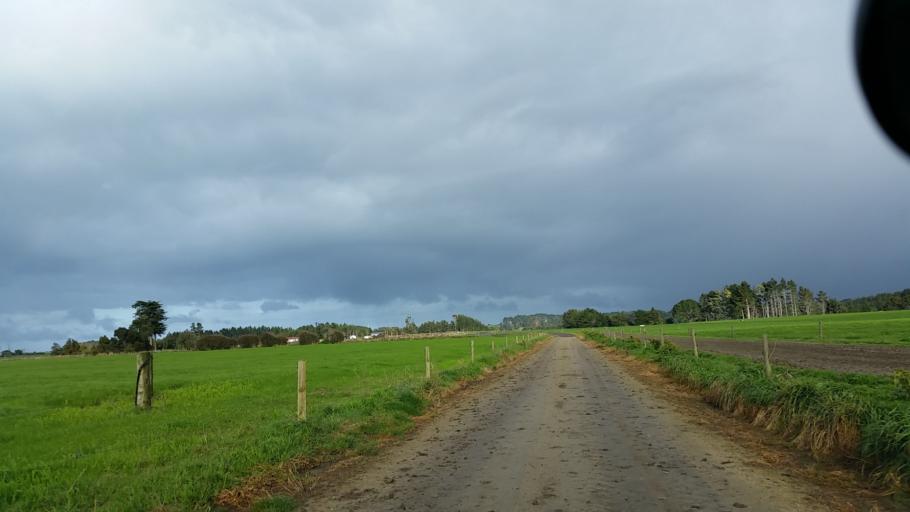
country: NZ
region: Taranaki
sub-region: South Taranaki District
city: Patea
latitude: -39.7324
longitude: 174.7025
